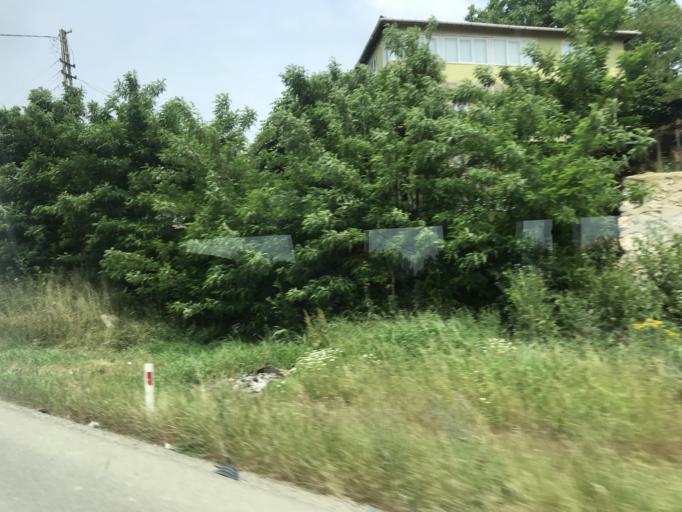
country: TR
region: Tekirdag
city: Inecik
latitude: 40.9375
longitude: 27.2808
